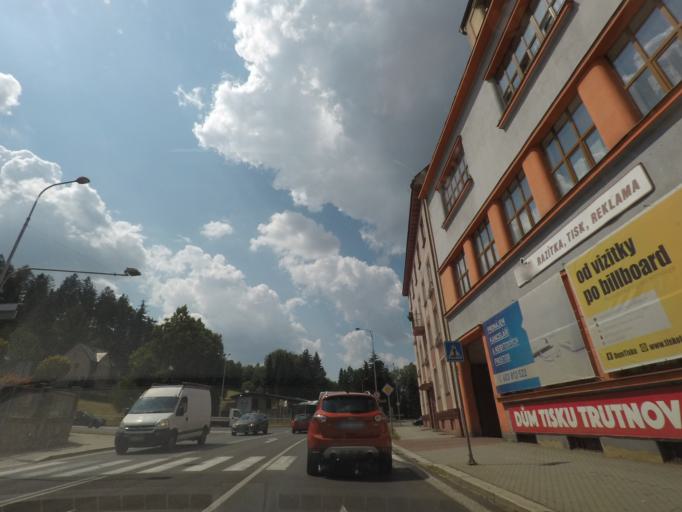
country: CZ
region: Kralovehradecky
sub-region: Okres Trutnov
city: Trutnov
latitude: 50.5588
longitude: 15.9087
